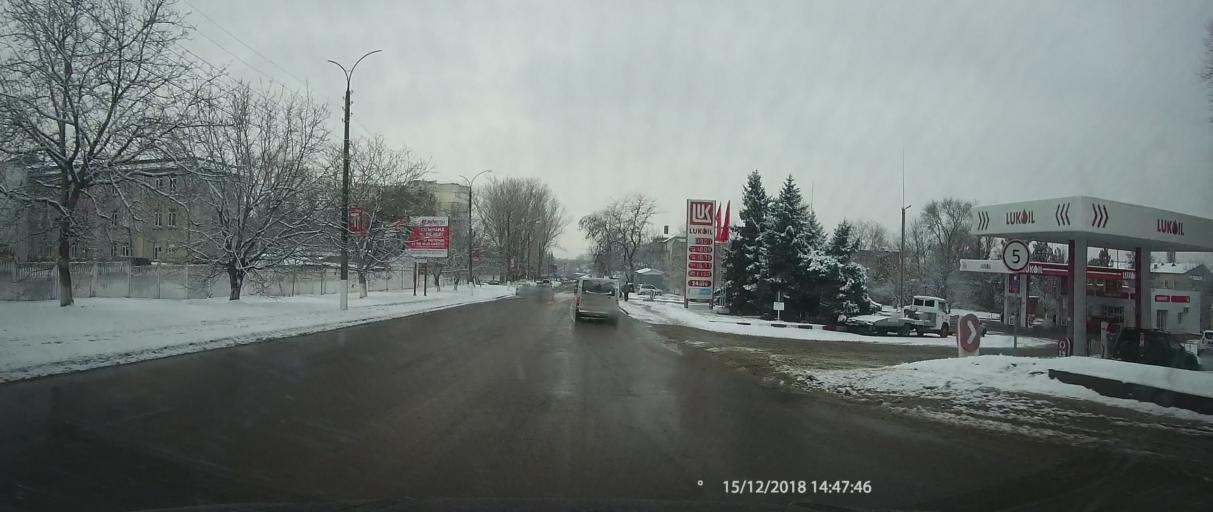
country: MD
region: Cahul
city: Cahul
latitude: 45.8956
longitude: 28.2032
